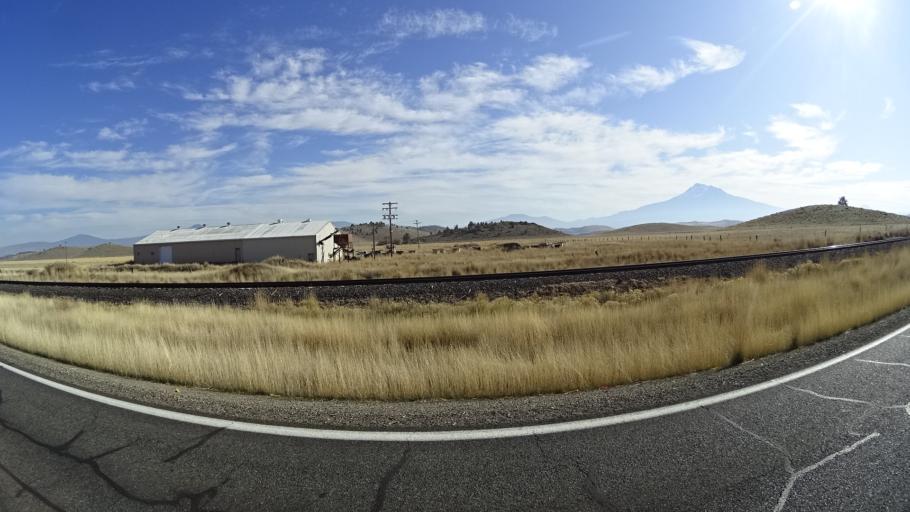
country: US
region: California
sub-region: Siskiyou County
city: Montague
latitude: 41.5830
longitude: -122.5246
